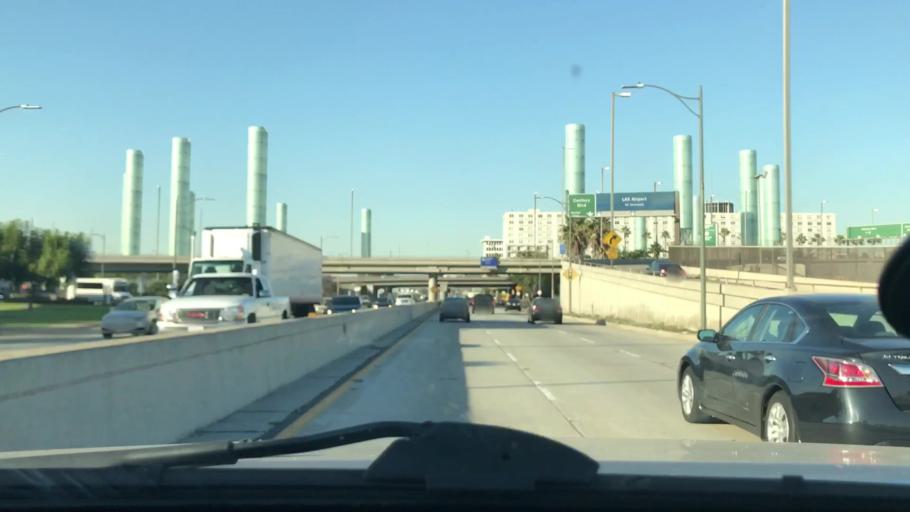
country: US
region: California
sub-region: Los Angeles County
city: El Segundo
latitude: 33.9424
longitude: -118.3962
